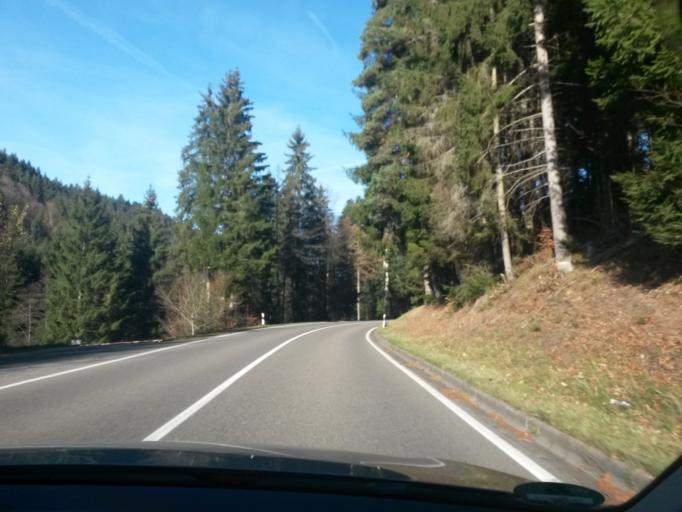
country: DE
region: Baden-Wuerttemberg
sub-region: Karlsruhe Region
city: Bad Wildbad
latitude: 48.7279
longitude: 8.5720
